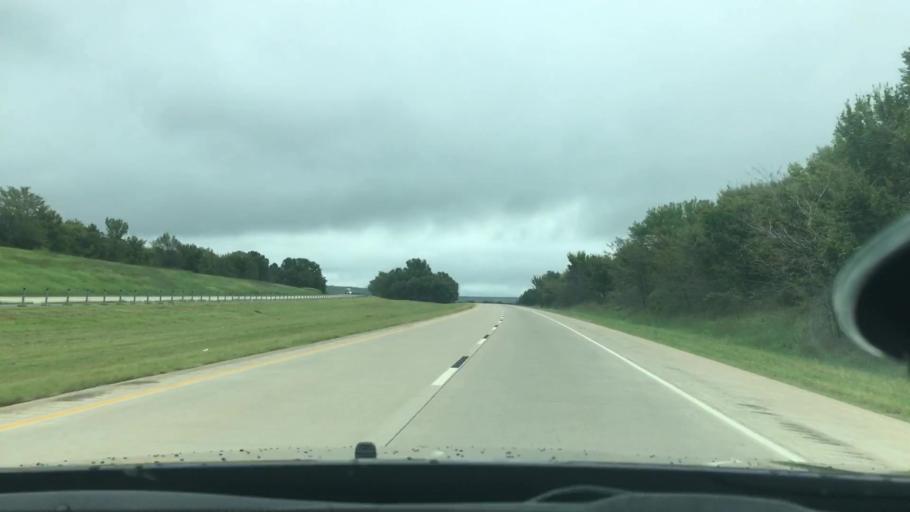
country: US
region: Oklahoma
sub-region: Okmulgee County
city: Henryetta
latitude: 35.4293
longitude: -95.9053
